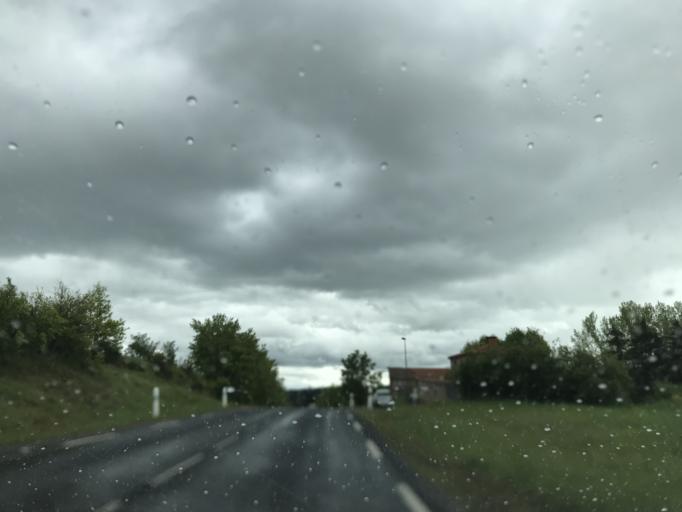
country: FR
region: Auvergne
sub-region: Departement du Puy-de-Dome
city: Billom
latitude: 45.7089
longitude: 3.4091
